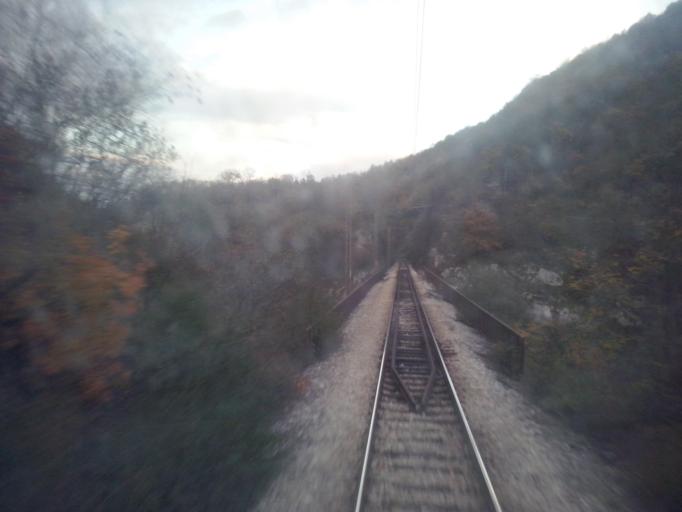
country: RS
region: Central Serbia
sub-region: Kolubarski Okrug
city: Valjevo
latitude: 44.2206
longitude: 19.8589
